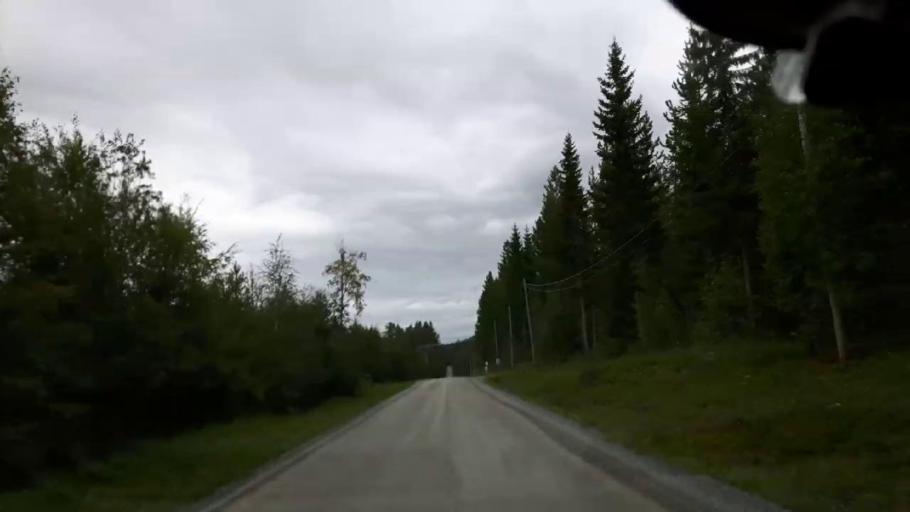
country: SE
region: Jaemtland
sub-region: Braecke Kommun
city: Braecke
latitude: 63.0945
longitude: 15.2479
